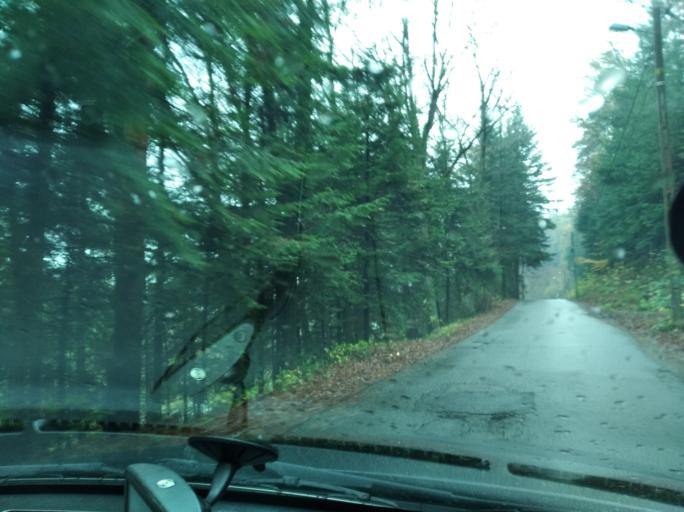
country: PL
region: Subcarpathian Voivodeship
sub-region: Powiat strzyzowski
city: Babica
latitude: 49.9314
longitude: 21.8966
